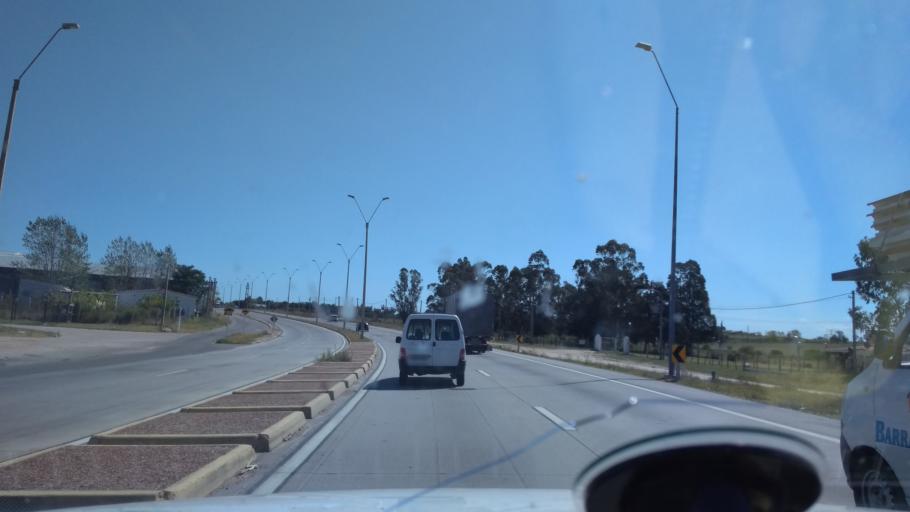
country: UY
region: Canelones
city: Toledo
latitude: -34.7904
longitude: -56.1098
